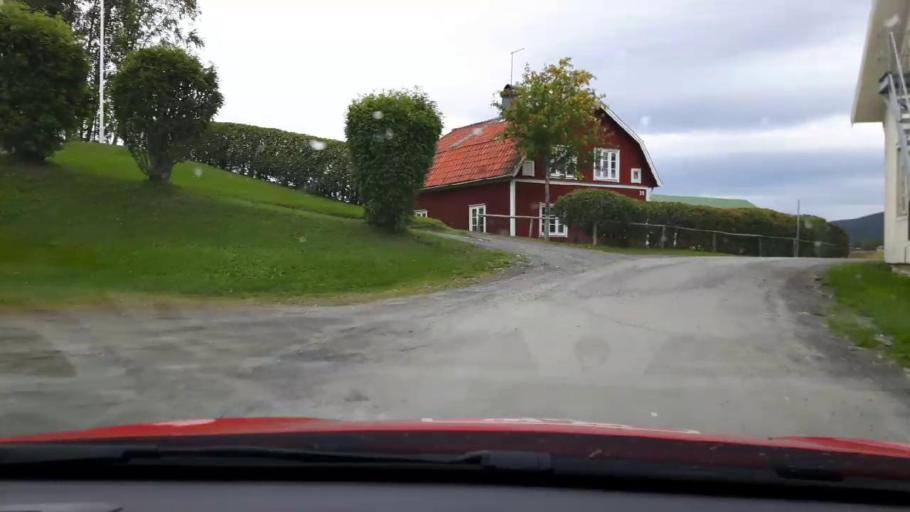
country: SE
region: Jaemtland
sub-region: Are Kommun
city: Are
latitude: 63.4906
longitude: 13.1206
